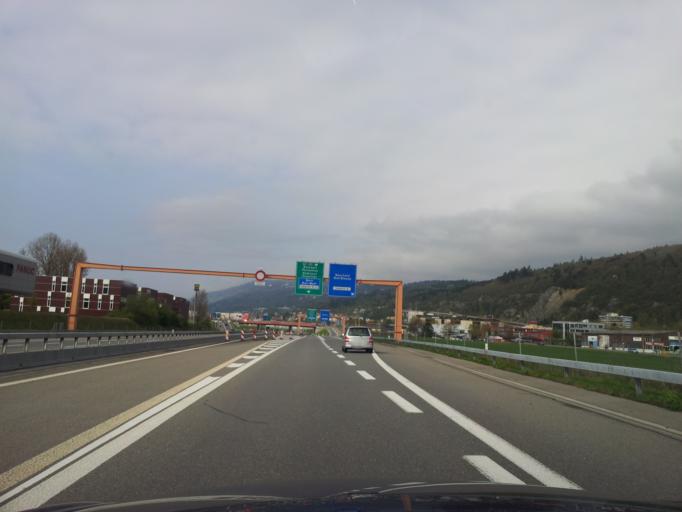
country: CH
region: Bern
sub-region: Biel/Bienne District
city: Orpund
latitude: 47.1603
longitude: 7.2911
